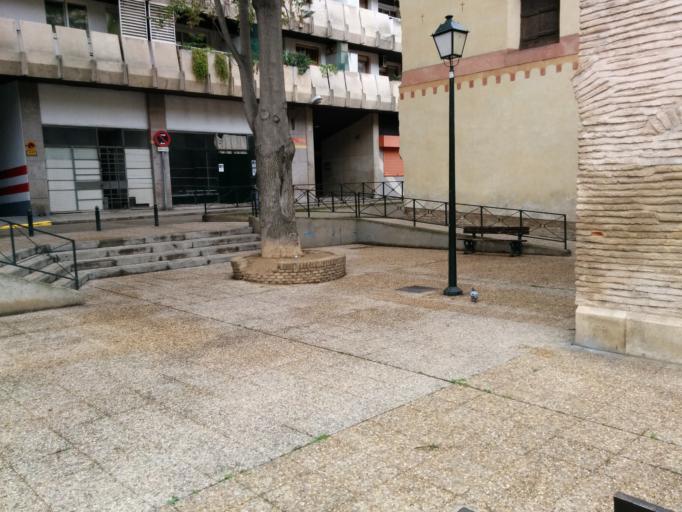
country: ES
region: Aragon
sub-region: Provincia de Zaragoza
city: Almozara
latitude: 41.6583
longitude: -0.8915
